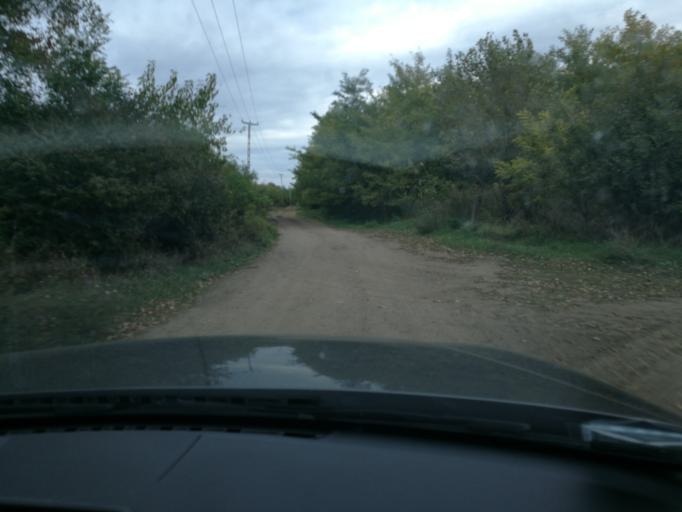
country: HU
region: Szabolcs-Szatmar-Bereg
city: Nyirpazony
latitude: 47.9972
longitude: 21.7932
